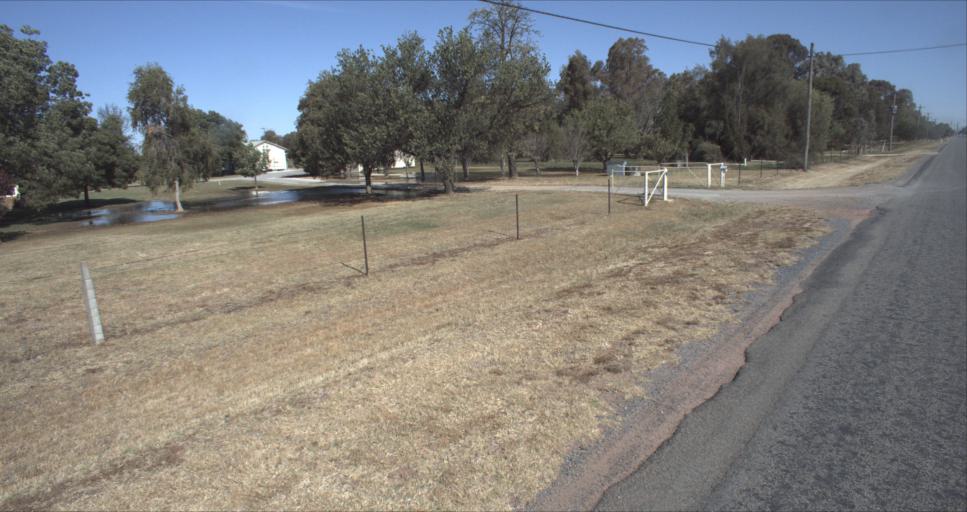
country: AU
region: New South Wales
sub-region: Leeton
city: Leeton
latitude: -34.5389
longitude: 146.4195
